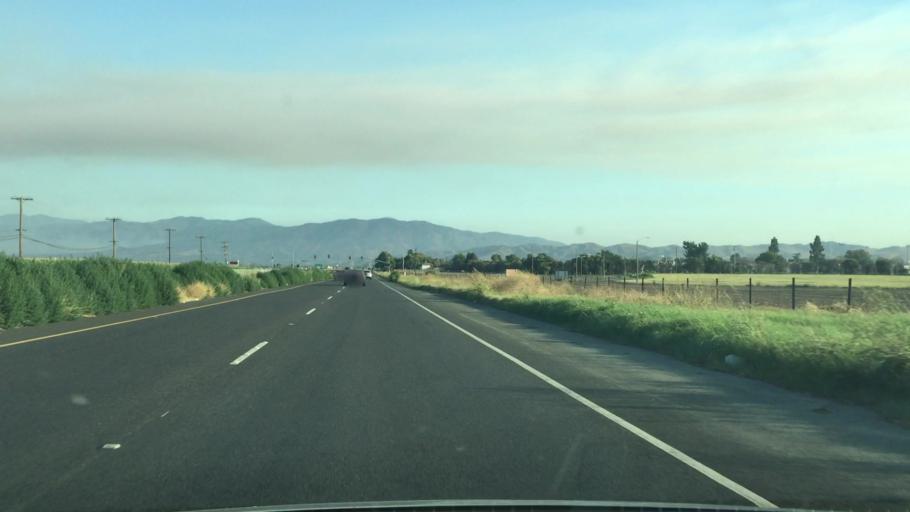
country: US
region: California
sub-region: San Bernardino County
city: Chino
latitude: 33.9863
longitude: -117.6509
